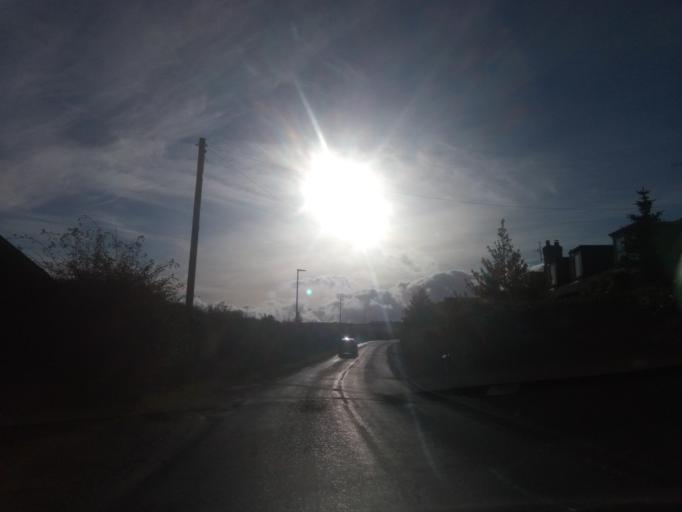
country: GB
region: Scotland
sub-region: The Scottish Borders
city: Eyemouth
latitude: 55.8618
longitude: -2.1006
